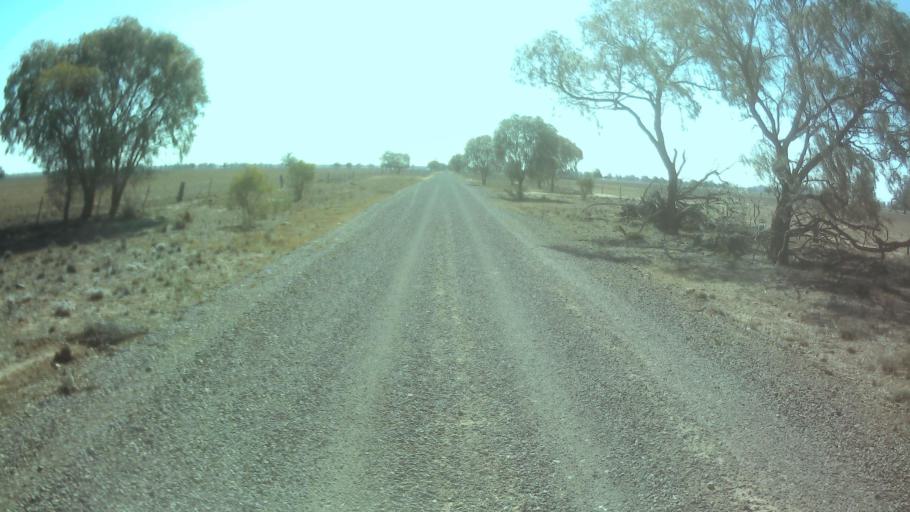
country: AU
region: New South Wales
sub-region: Weddin
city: Grenfell
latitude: -33.7611
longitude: 147.7181
